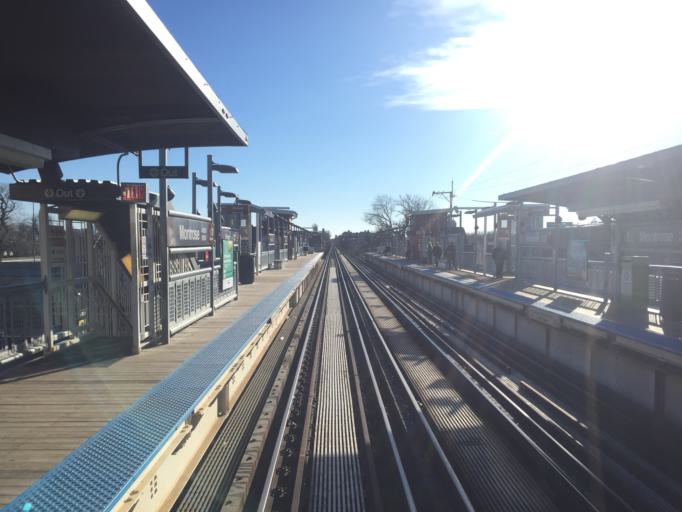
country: US
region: Illinois
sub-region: Cook County
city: Lincolnwood
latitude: 41.9617
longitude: -87.6751
